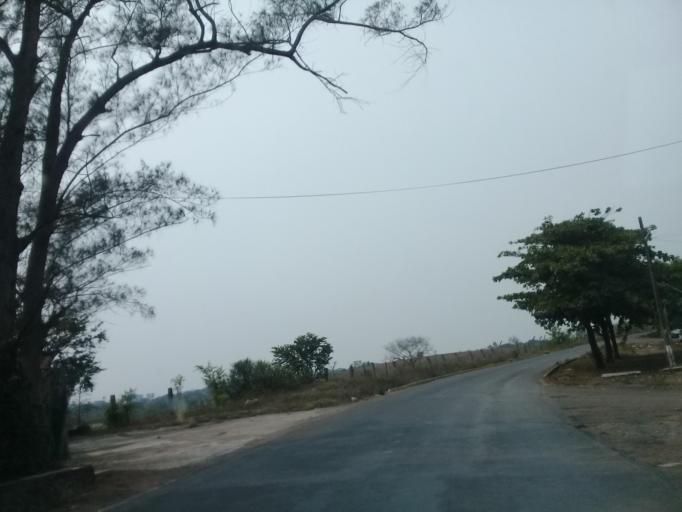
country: MX
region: Veracruz
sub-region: Medellin
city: La Laguna y Monte del Castillo
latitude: 18.9720
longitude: -96.1198
